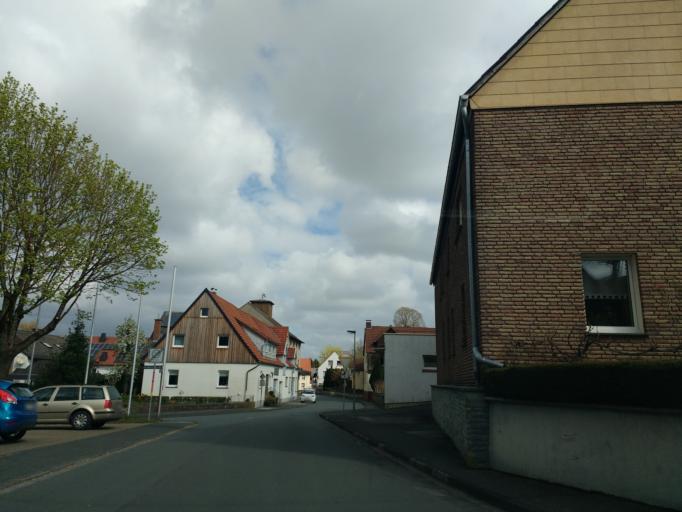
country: DE
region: North Rhine-Westphalia
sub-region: Regierungsbezirk Detmold
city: Wunnenberg
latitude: 51.5141
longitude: 8.7420
